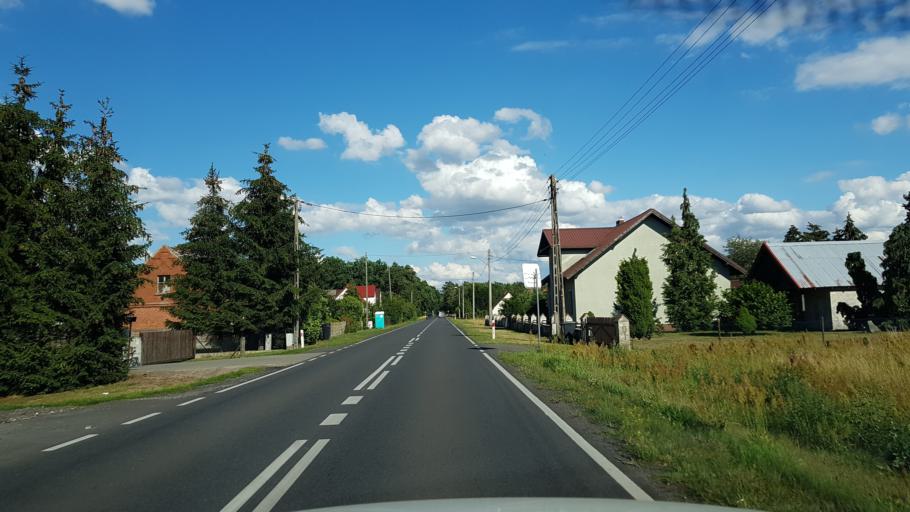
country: PL
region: West Pomeranian Voivodeship
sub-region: Powiat goleniowski
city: Goleniow
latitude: 53.5761
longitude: 14.7729
